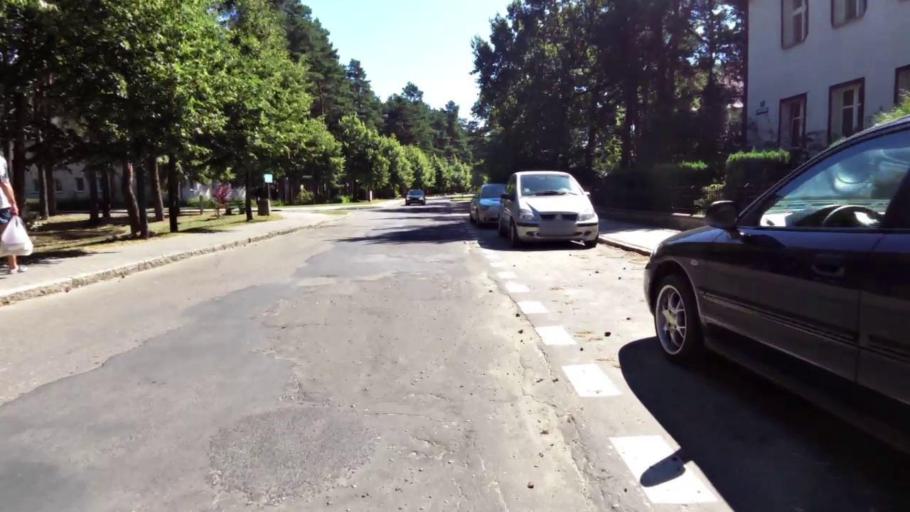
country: PL
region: West Pomeranian Voivodeship
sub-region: Powiat szczecinecki
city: Borne Sulinowo
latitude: 53.5857
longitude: 16.5414
